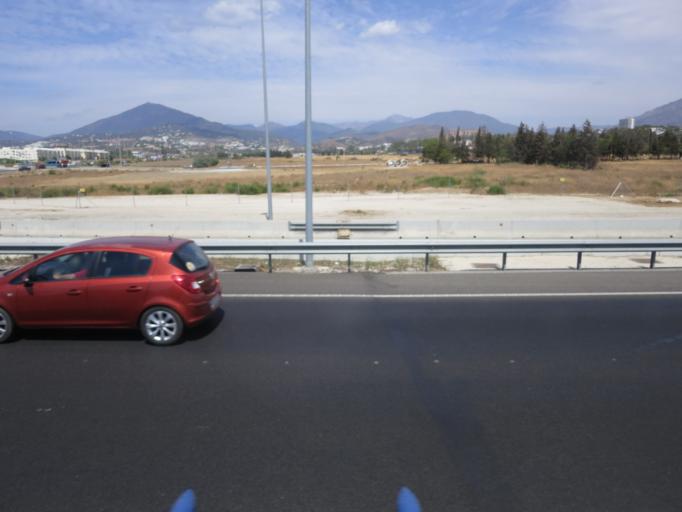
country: ES
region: Andalusia
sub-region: Provincia de Malaga
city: Benahavis
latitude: 36.4853
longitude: -4.9798
